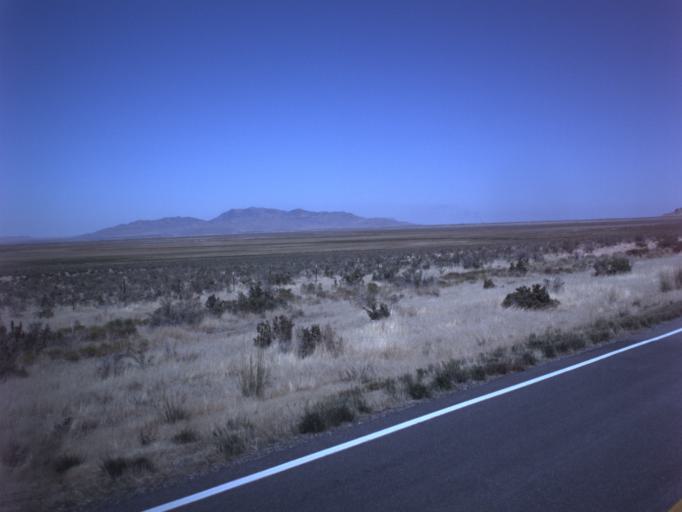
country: US
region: Utah
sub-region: Tooele County
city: Grantsville
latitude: 40.6314
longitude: -112.6947
